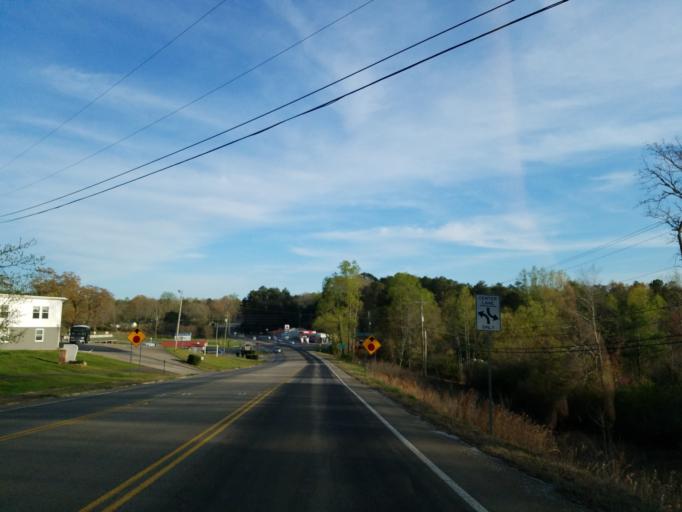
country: US
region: Georgia
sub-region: Pickens County
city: Nelson
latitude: 34.4152
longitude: -84.3902
